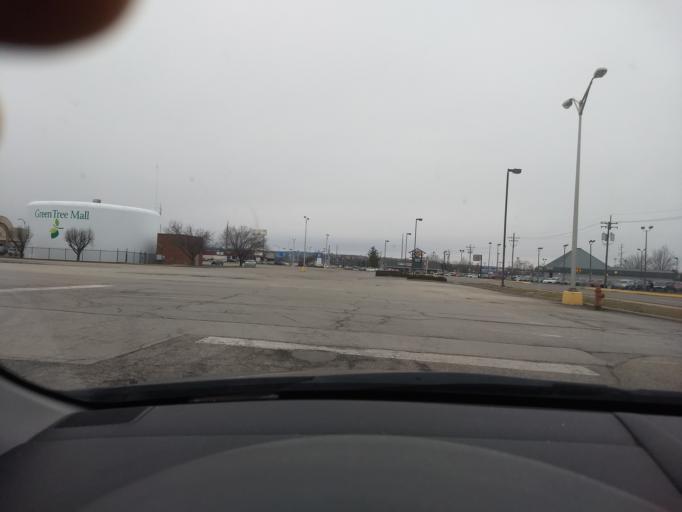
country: US
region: Indiana
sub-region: Clark County
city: Clarksville
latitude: 38.3171
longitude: -85.7625
